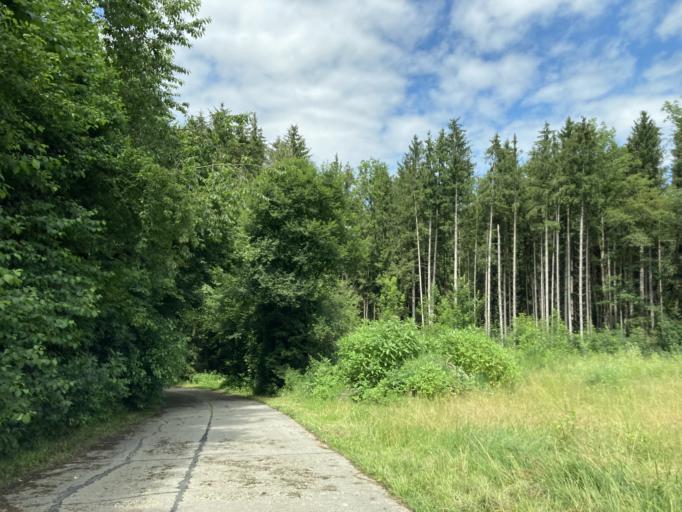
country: DE
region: Bavaria
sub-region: Upper Bavaria
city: Vogtareuth
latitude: 47.9460
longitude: 12.1717
